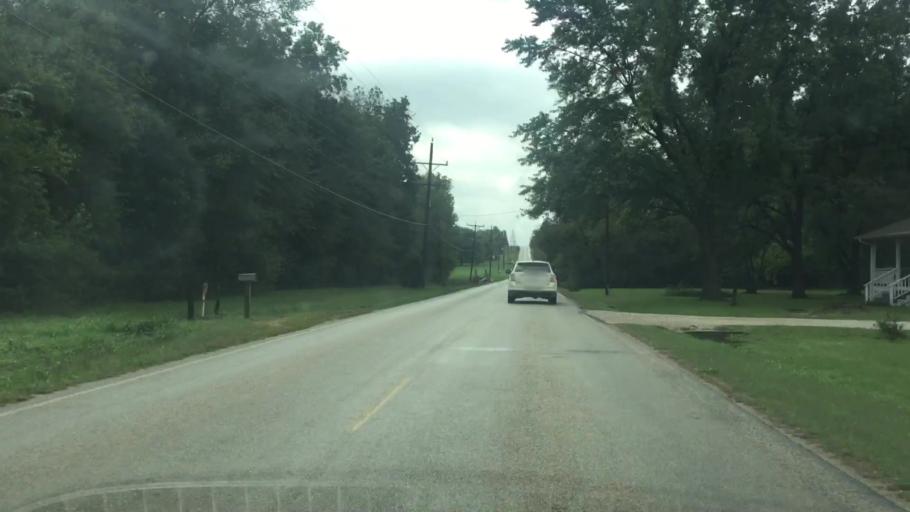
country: US
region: Kansas
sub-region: Allen County
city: Humboldt
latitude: 37.8676
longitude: -95.4369
